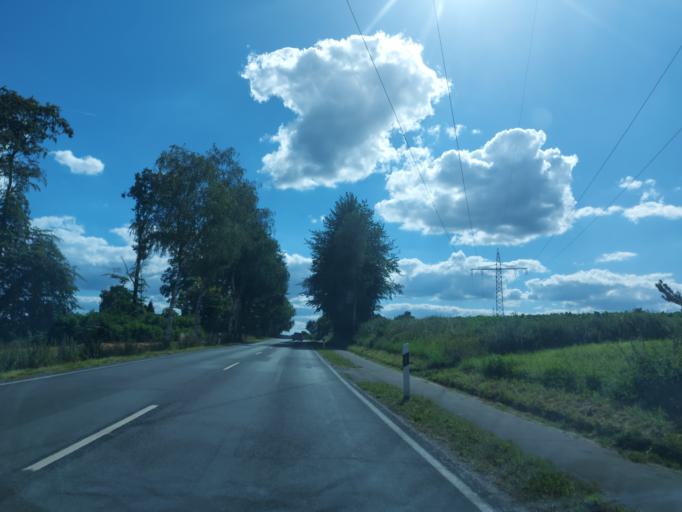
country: DE
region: Lower Saxony
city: Hagen
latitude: 52.2079
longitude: 7.9896
